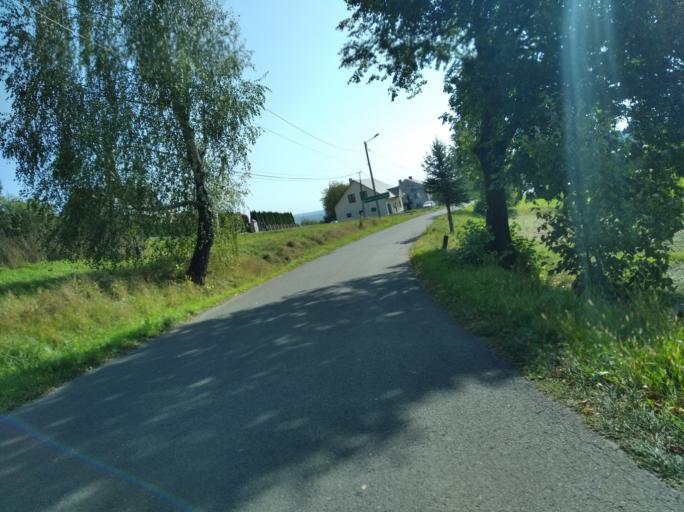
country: PL
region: Subcarpathian Voivodeship
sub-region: Powiat strzyzowski
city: Czudec
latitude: 49.9521
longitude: 21.8331
